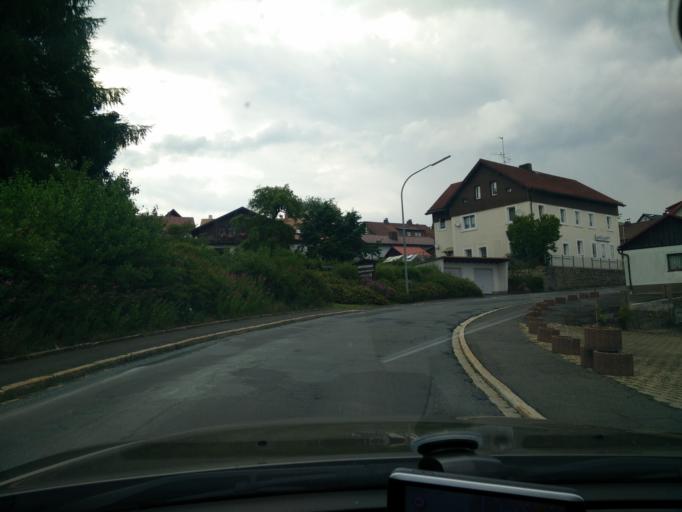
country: DE
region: Bavaria
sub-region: Upper Franconia
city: Fichtelberg
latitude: 50.0075
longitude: 11.8499
